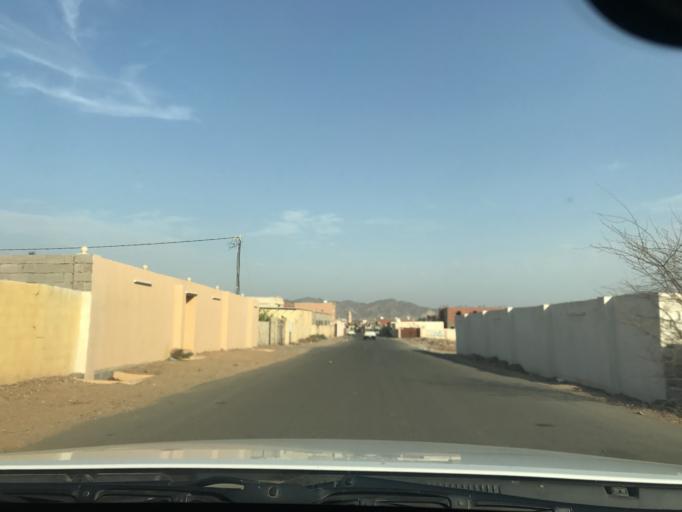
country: SA
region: Makkah
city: Al Jumum
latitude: 21.4433
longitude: 39.5184
